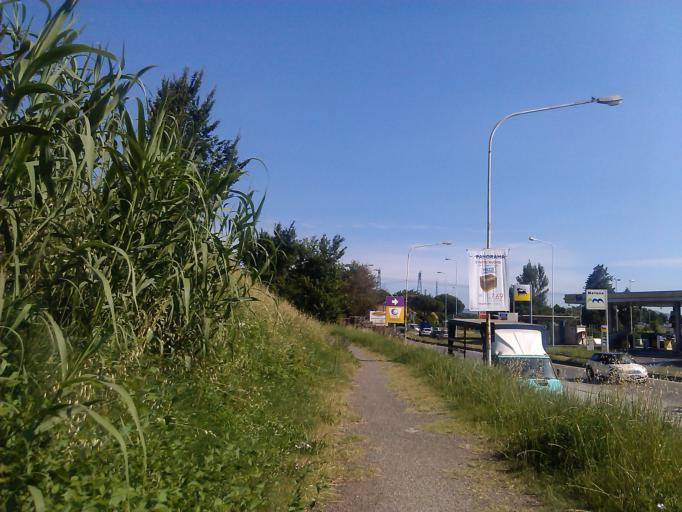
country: IT
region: Tuscany
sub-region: Province of Florence
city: Campi Bisenzio
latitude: 43.8566
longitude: 11.1230
